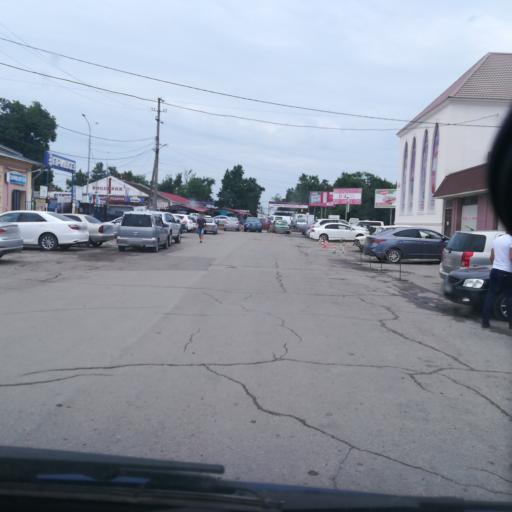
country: RU
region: Krasnodarskiy
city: Slavyansk-na-Kubani
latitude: 45.2629
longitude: 38.1302
